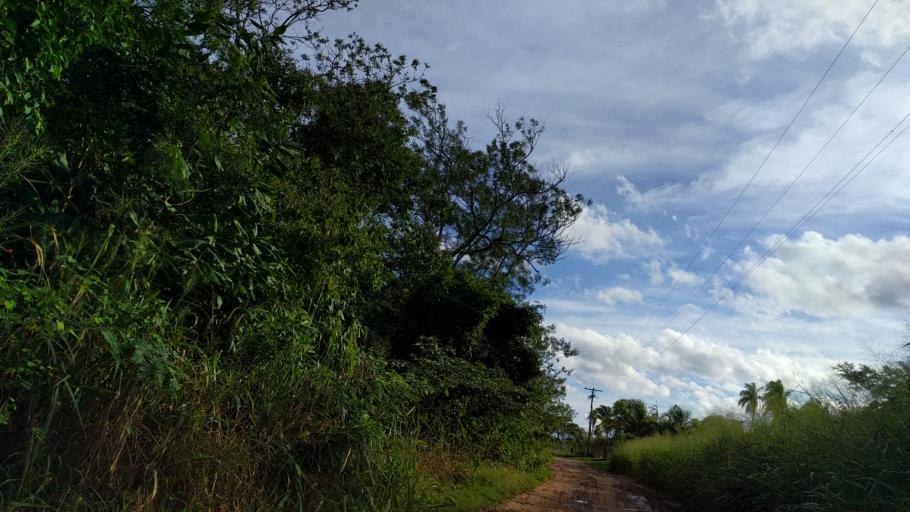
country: BO
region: Santa Cruz
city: Santa Cruz de la Sierra
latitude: -17.8531
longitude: -63.2628
